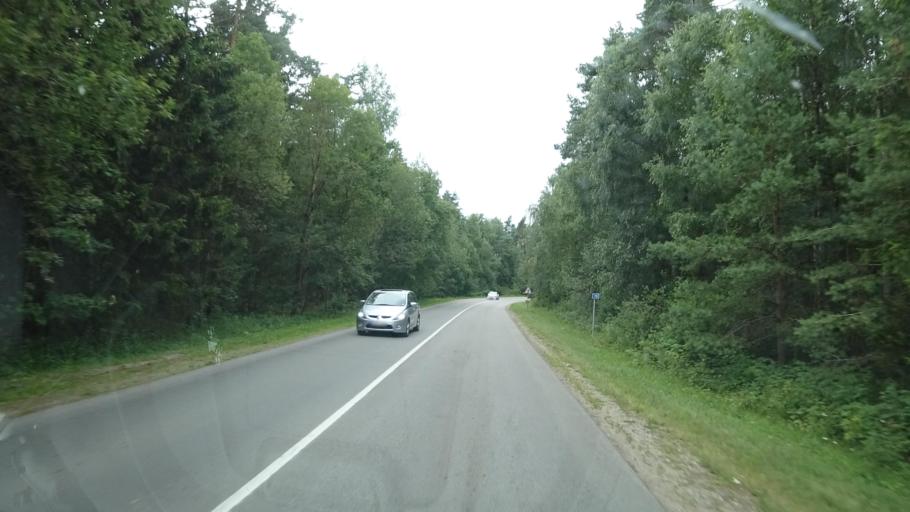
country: LT
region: Klaipedos apskritis
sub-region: Palanga
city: Sventoji
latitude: 56.0113
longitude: 21.1088
